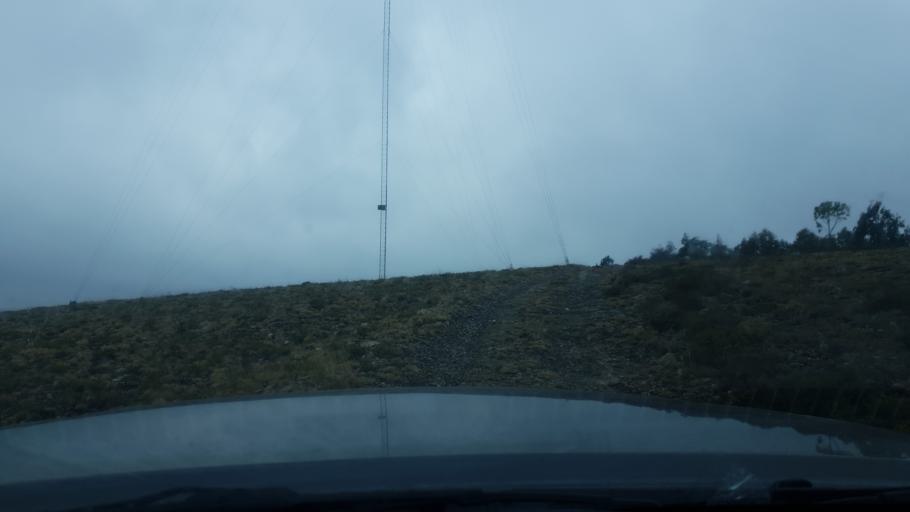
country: PT
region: Viseu
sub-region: Sao Pedro do Sul
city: Sao Pedro do Sul
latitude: 40.8611
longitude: -8.0949
